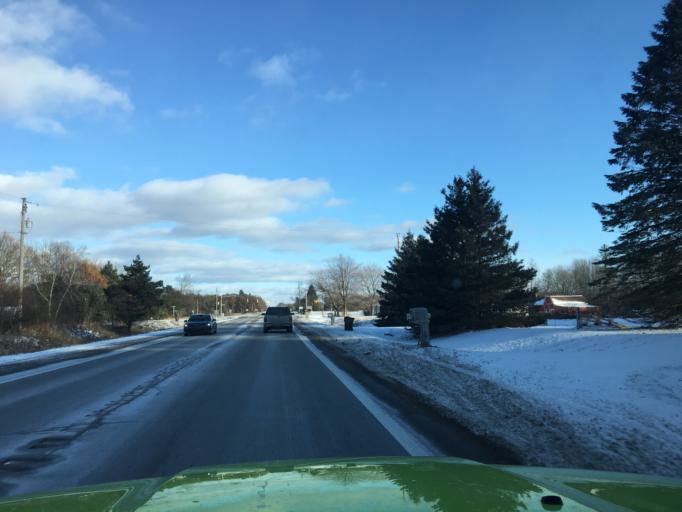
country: US
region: Michigan
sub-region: Kent County
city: Cedar Springs
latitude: 43.1757
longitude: -85.4938
